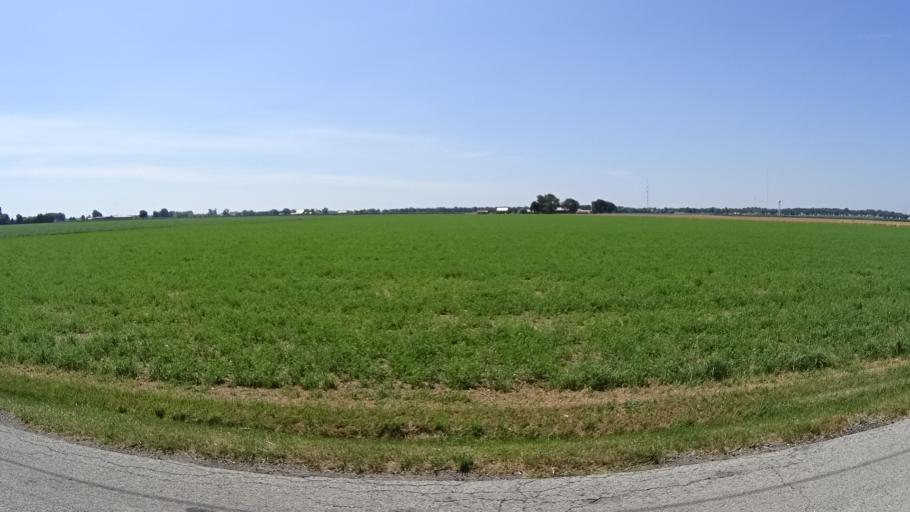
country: US
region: Ohio
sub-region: Erie County
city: Sandusky
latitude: 41.4251
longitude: -82.7852
